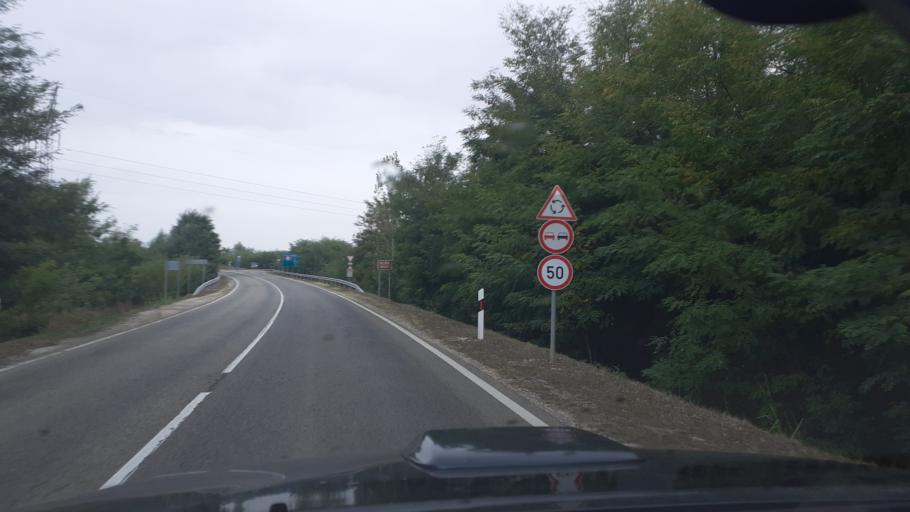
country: HU
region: Fejer
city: Baracs
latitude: 46.8543
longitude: 18.8786
